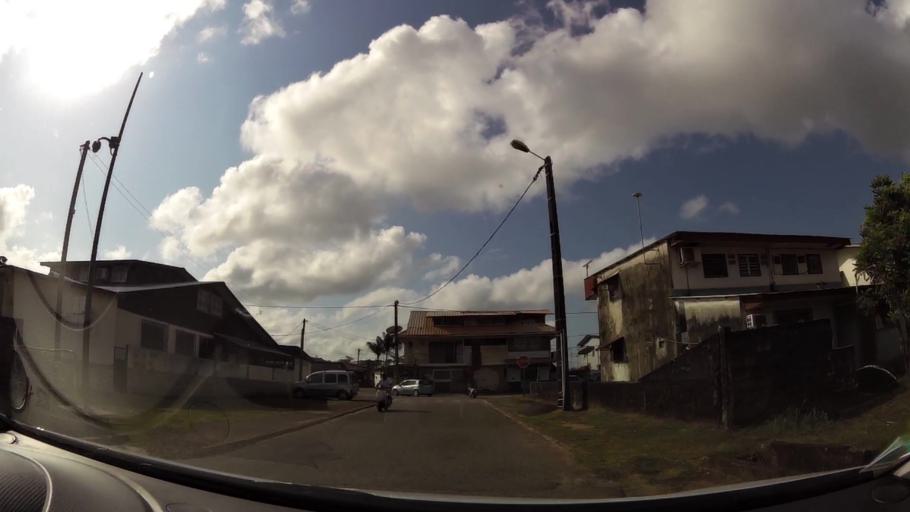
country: GF
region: Guyane
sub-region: Guyane
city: Cayenne
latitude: 4.9317
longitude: -52.3249
